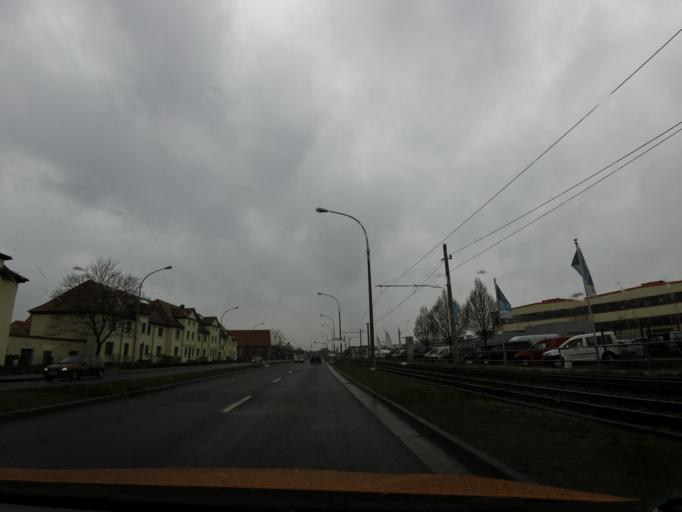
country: DE
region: Brandenburg
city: Brandenburg an der Havel
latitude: 52.4137
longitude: 12.5131
